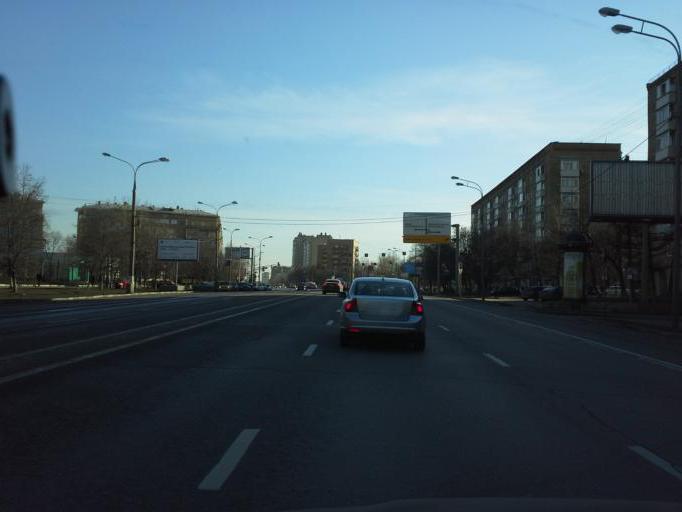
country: RU
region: Moscow
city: Taganskiy
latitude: 55.7200
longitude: 37.6635
